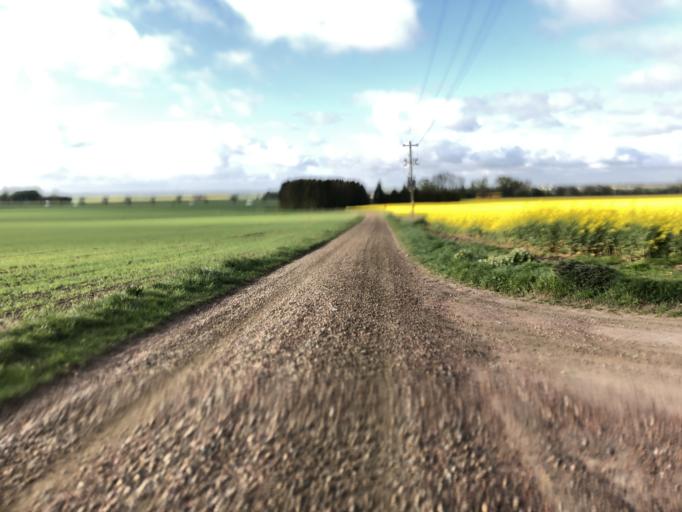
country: SE
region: Skane
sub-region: Staffanstorps Kommun
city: Staffanstorp
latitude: 55.6876
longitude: 13.2693
